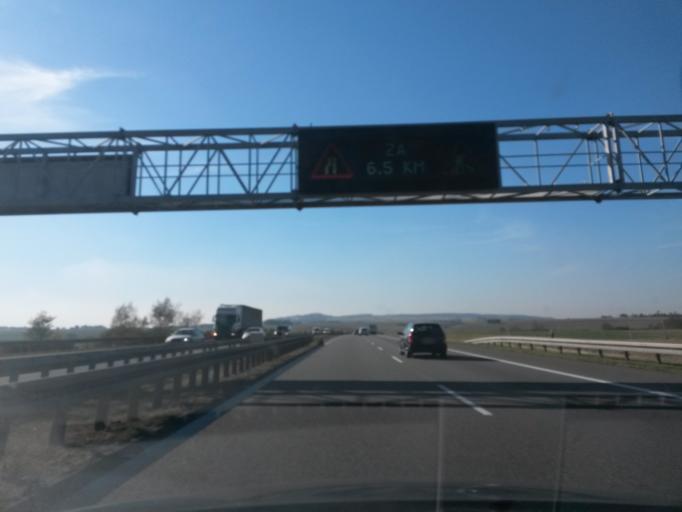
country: PL
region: Opole Voivodeship
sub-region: Powiat strzelecki
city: Lesnica
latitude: 50.4587
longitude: 18.2496
